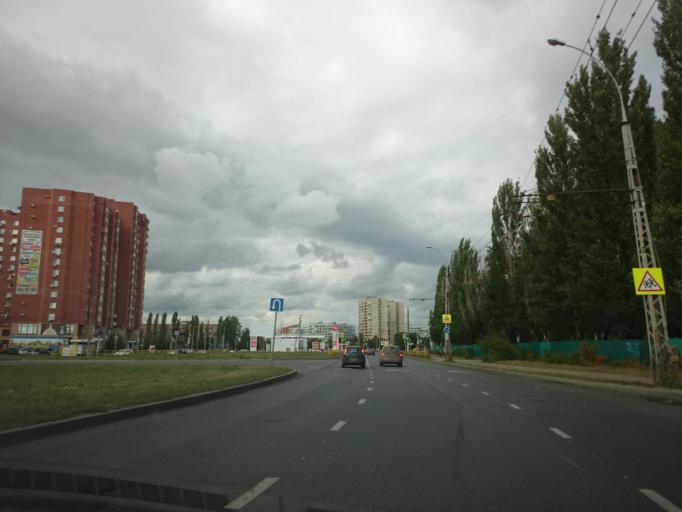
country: RU
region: Samara
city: Tol'yatti
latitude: 53.5147
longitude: 49.3080
